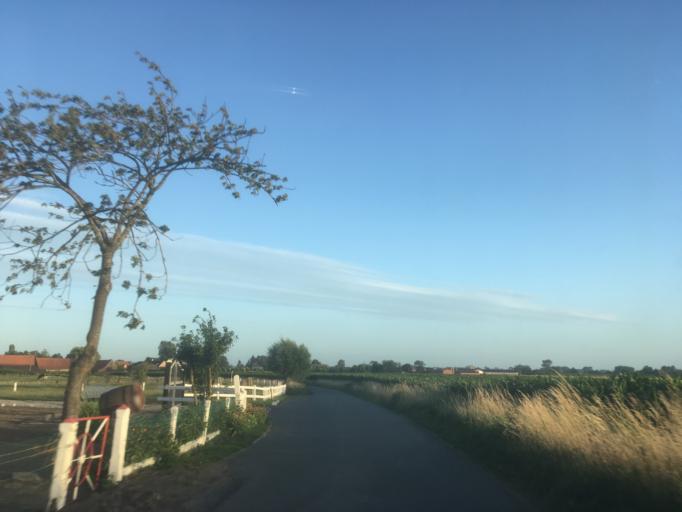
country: BE
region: Flanders
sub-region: Provincie West-Vlaanderen
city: Torhout
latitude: 51.0479
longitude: 3.0868
